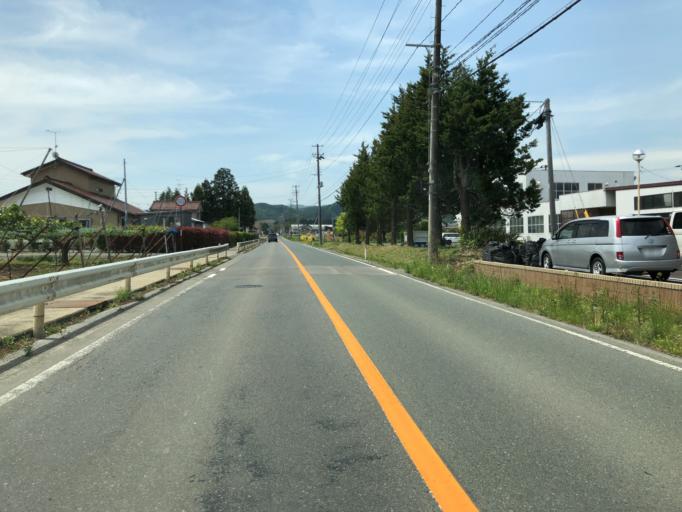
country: JP
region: Fukushima
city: Namie
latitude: 37.6928
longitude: 140.9421
